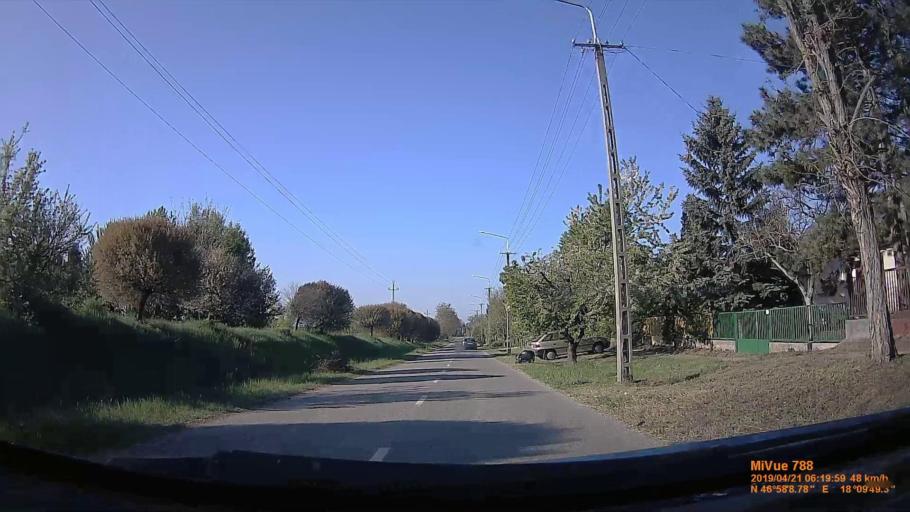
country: HU
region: Somogy
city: Balatonszabadi
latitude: 46.9691
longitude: 18.1637
